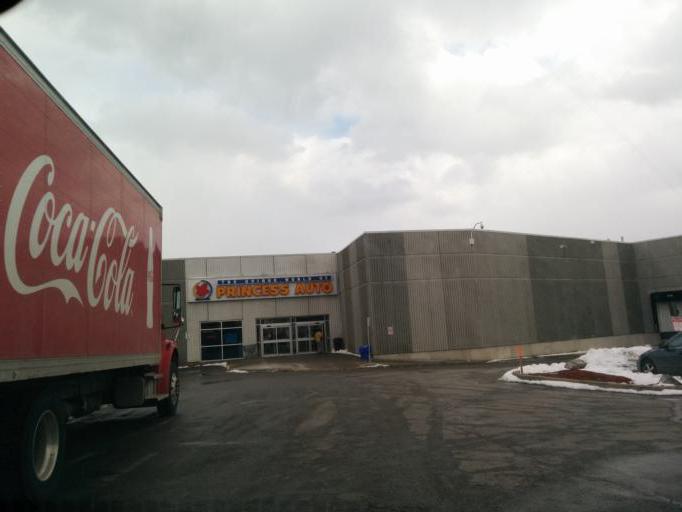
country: CA
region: Ontario
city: Mississauga
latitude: 43.6670
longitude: -79.6654
